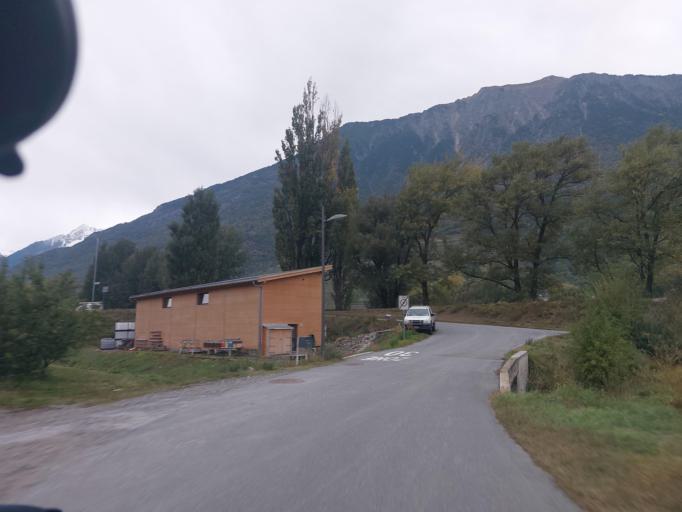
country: CH
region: Valais
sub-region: Martigny District
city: Fully
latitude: 46.1348
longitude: 7.1228
